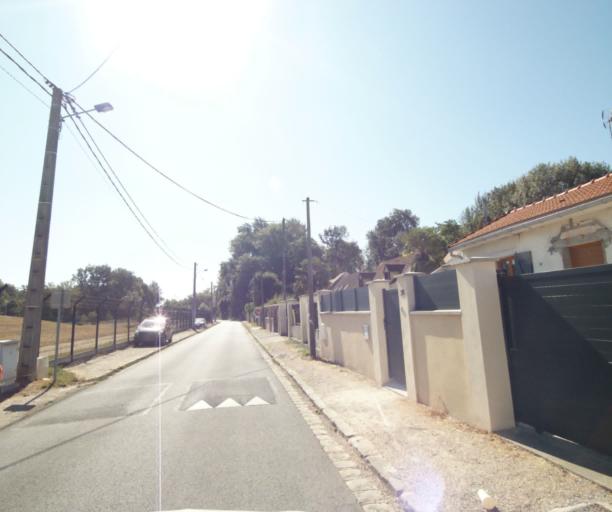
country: FR
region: Ile-de-France
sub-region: Departement de l'Essonne
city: Vert-le-Petit
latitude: 48.5343
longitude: 2.3567
